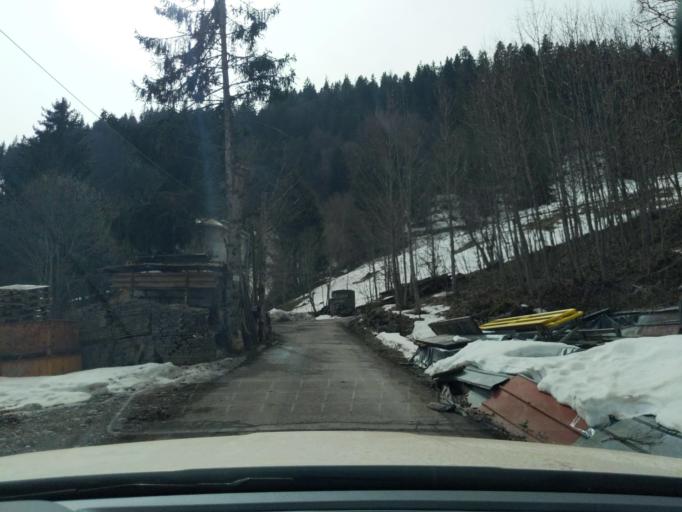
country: DE
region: Bavaria
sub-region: Swabia
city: Obermaiselstein
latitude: 47.4389
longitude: 10.2323
